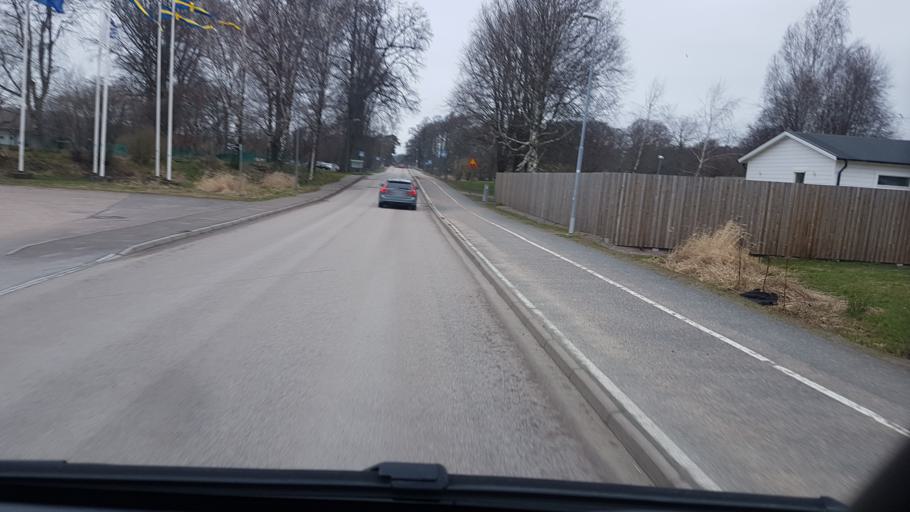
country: SE
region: Vaestra Goetaland
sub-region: Lerums Kommun
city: Lerum
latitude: 57.7645
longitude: 12.2576
